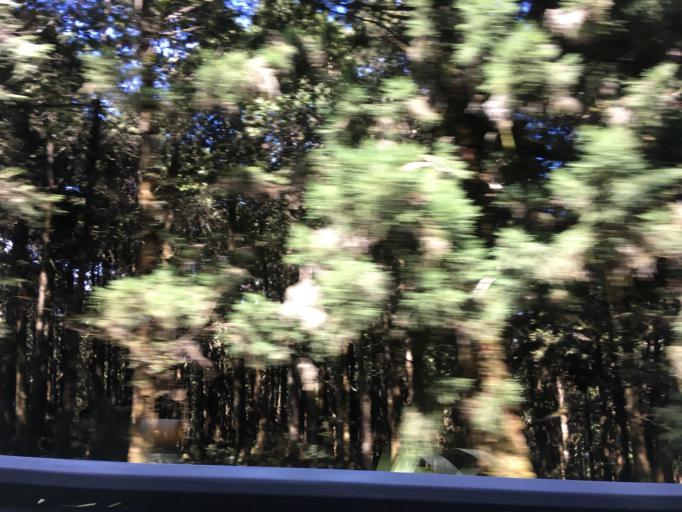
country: TW
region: Taiwan
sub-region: Yilan
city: Yilan
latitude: 24.5167
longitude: 121.5214
